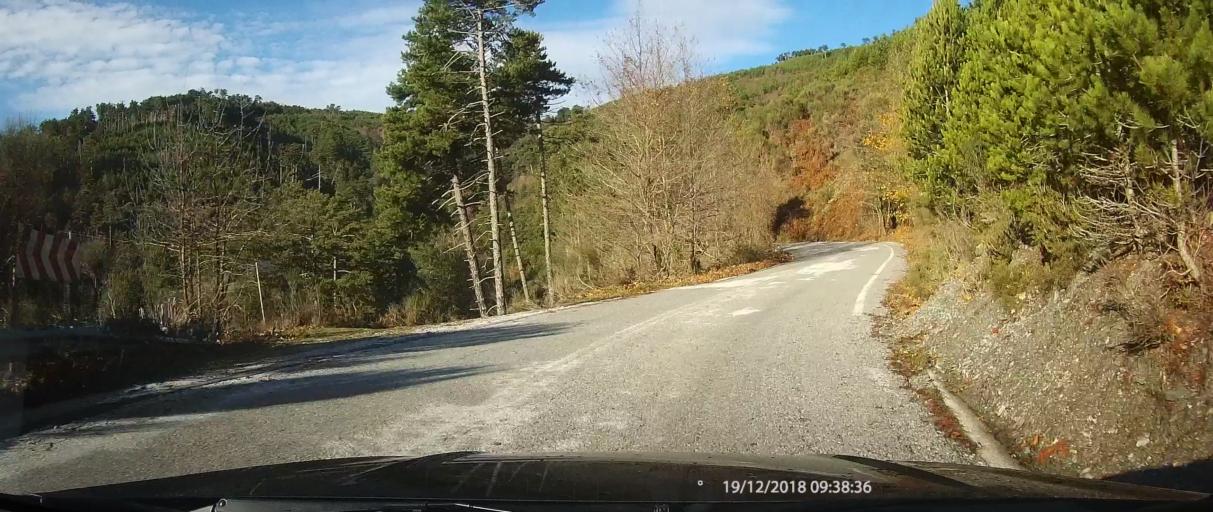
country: GR
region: Peloponnese
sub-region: Nomos Lakonias
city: Magoula
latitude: 37.0804
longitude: 22.2746
